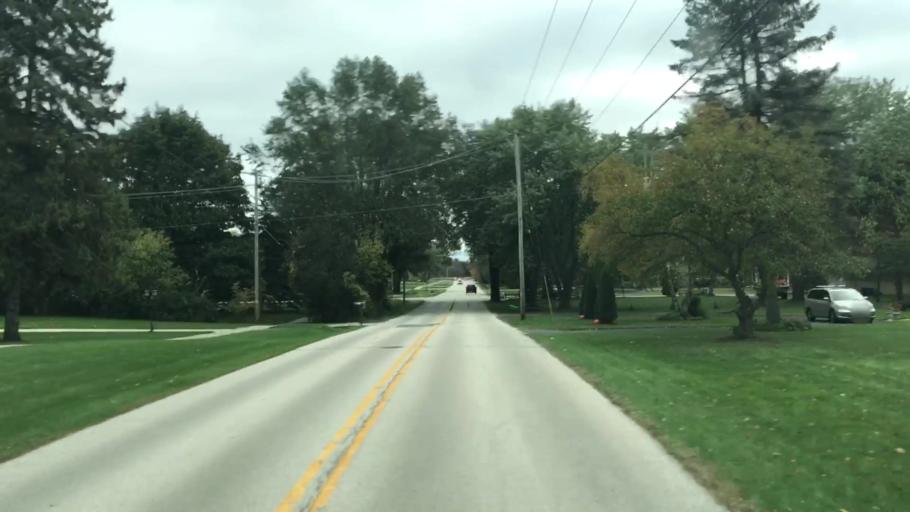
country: US
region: Wisconsin
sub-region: Waukesha County
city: Brookfield
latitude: 43.0758
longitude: -88.1341
